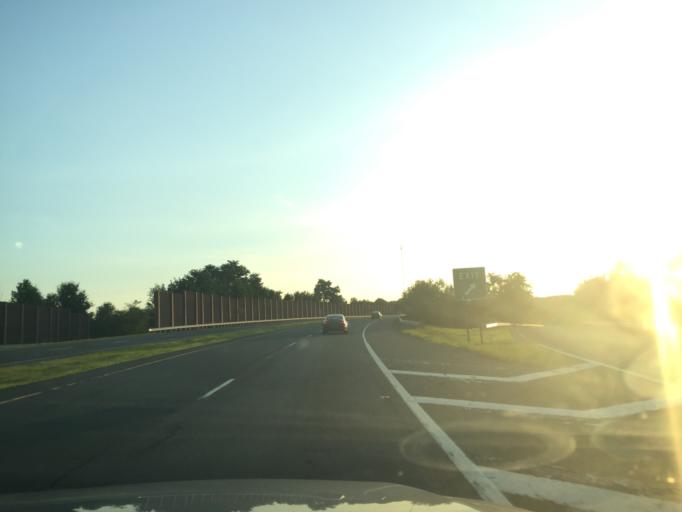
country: US
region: New Jersey
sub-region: Mercer County
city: Hightstown
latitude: 40.2821
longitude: -74.5421
